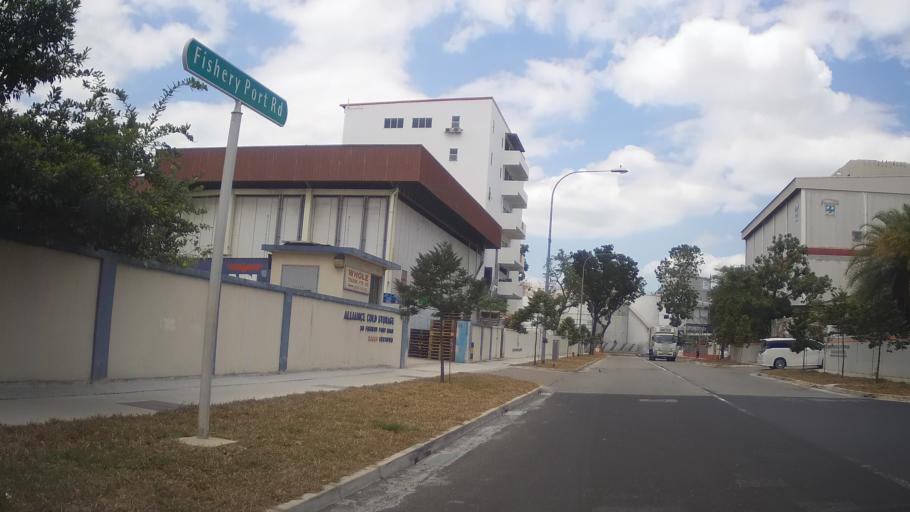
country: SG
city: Singapore
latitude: 1.3103
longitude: 103.7227
